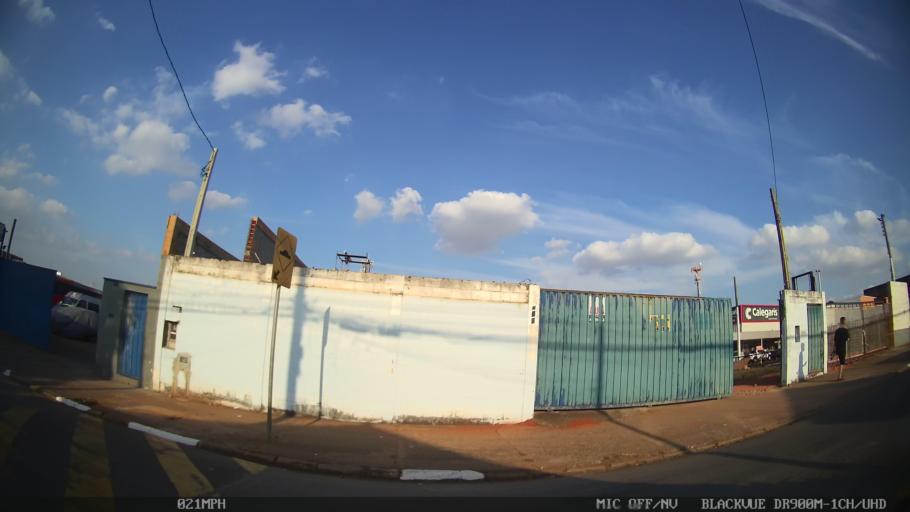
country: BR
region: Sao Paulo
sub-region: Hortolandia
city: Hortolandia
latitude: -22.8623
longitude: -47.1498
